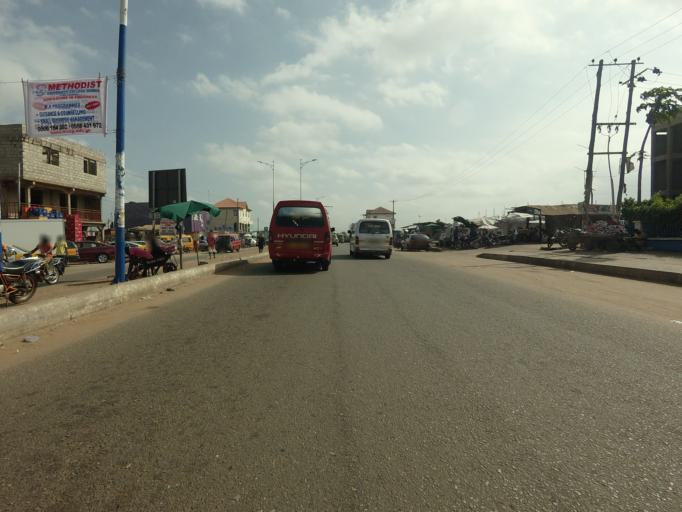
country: GH
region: Greater Accra
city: Tema
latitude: 5.6897
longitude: -0.0278
